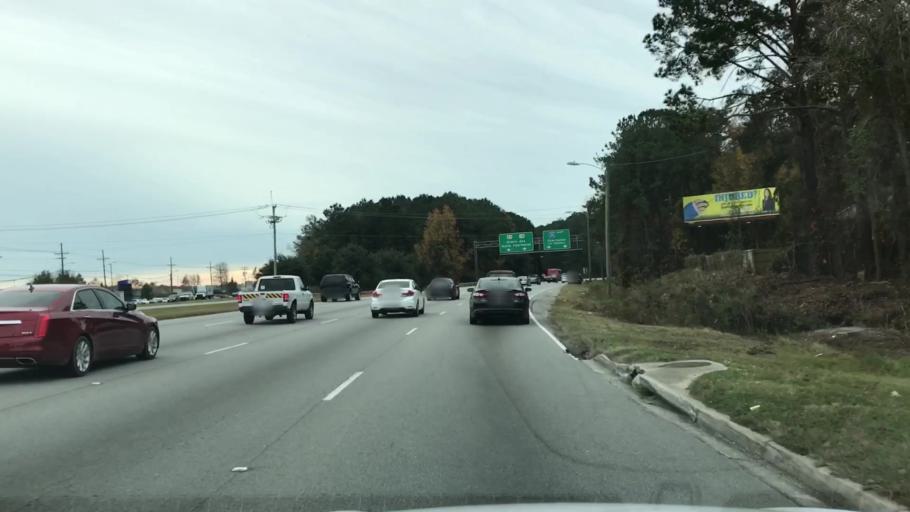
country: US
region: South Carolina
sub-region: Berkeley County
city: Goose Creek
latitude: 32.9526
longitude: -80.0425
